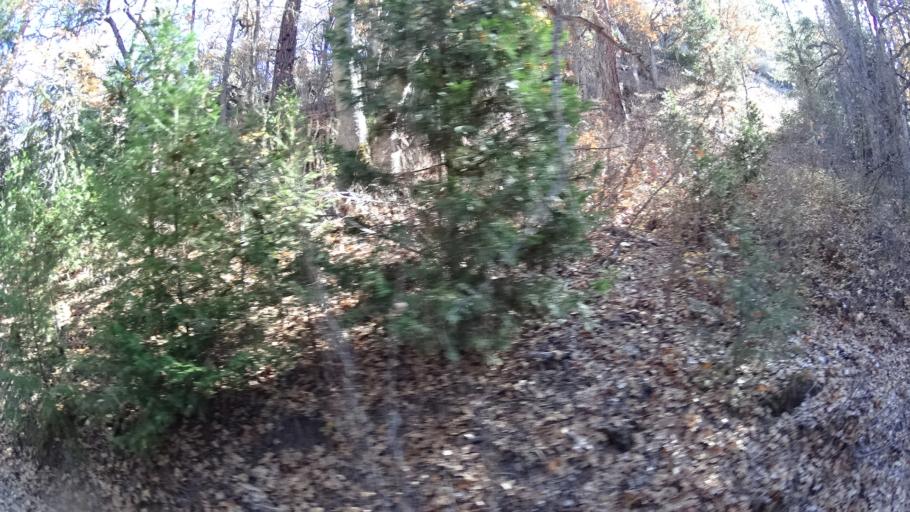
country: US
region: California
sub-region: Siskiyou County
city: Yreka
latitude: 41.8641
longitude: -122.7441
